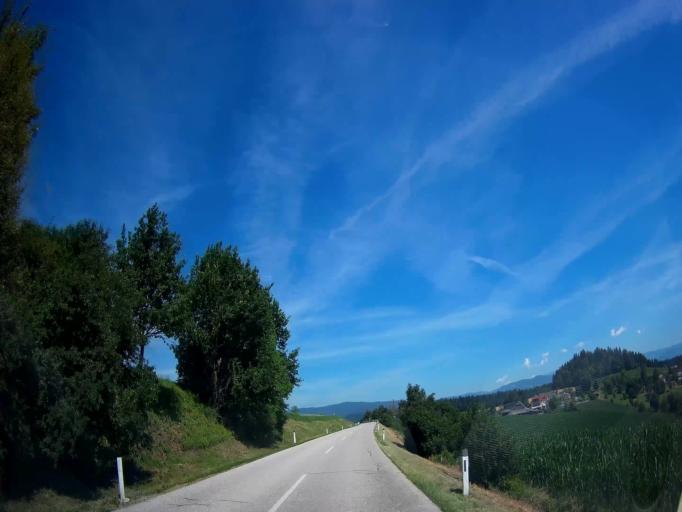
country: AT
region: Carinthia
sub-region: Politischer Bezirk Sankt Veit an der Glan
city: St. Georgen am Laengsee
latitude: 46.7920
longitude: 14.4182
